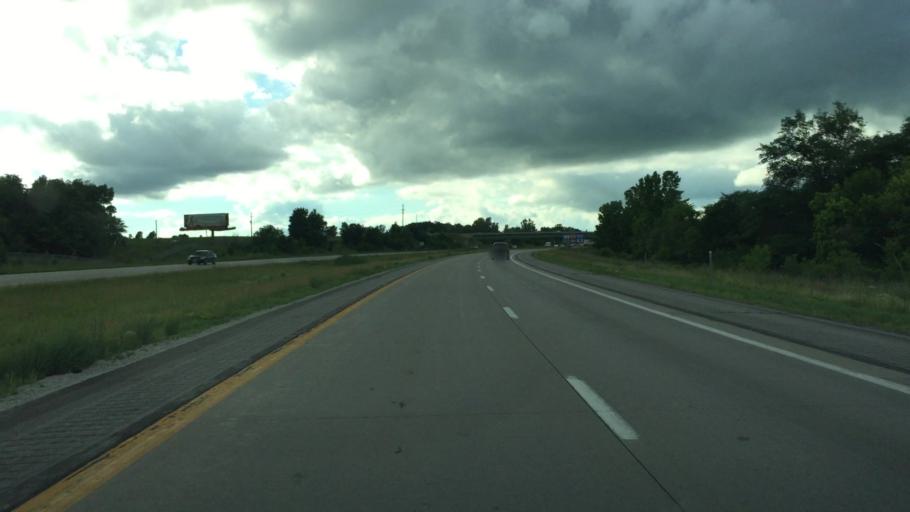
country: US
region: Iowa
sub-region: Polk County
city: Altoona
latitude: 41.6287
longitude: -93.4997
